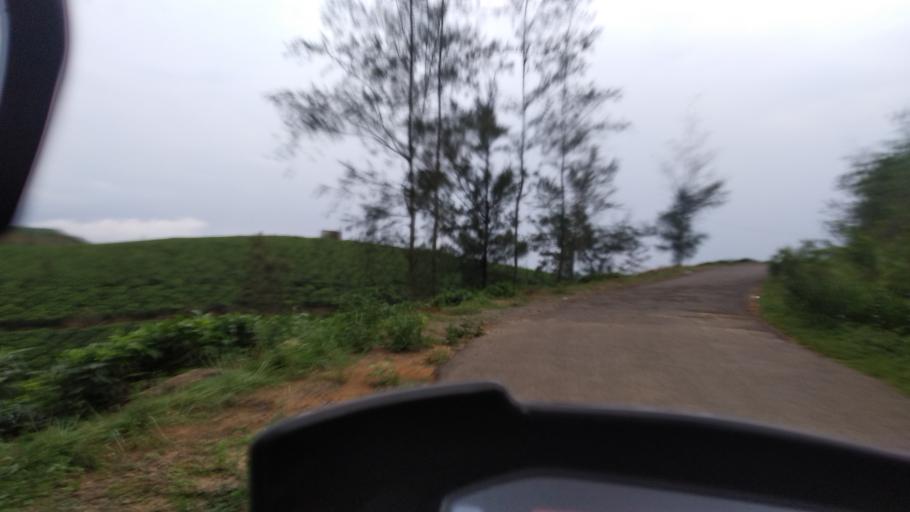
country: IN
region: Tamil Nadu
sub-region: Theni
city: Gudalur
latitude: 9.5448
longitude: 77.0380
